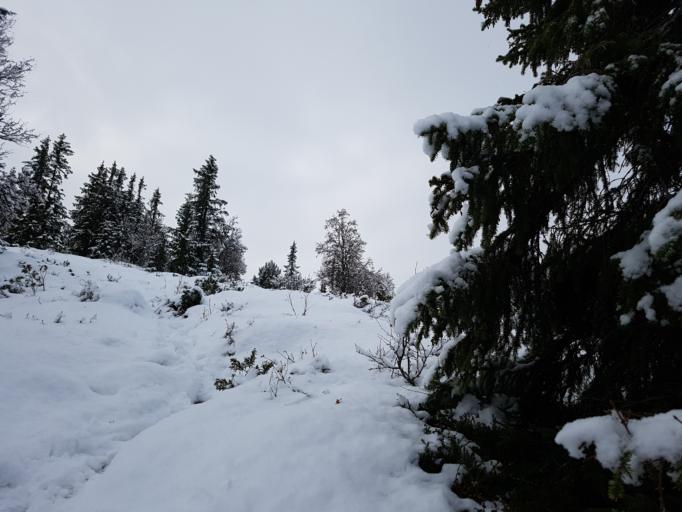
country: NO
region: Oppland
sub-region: Sel
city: Otta
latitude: 61.8054
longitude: 9.6775
